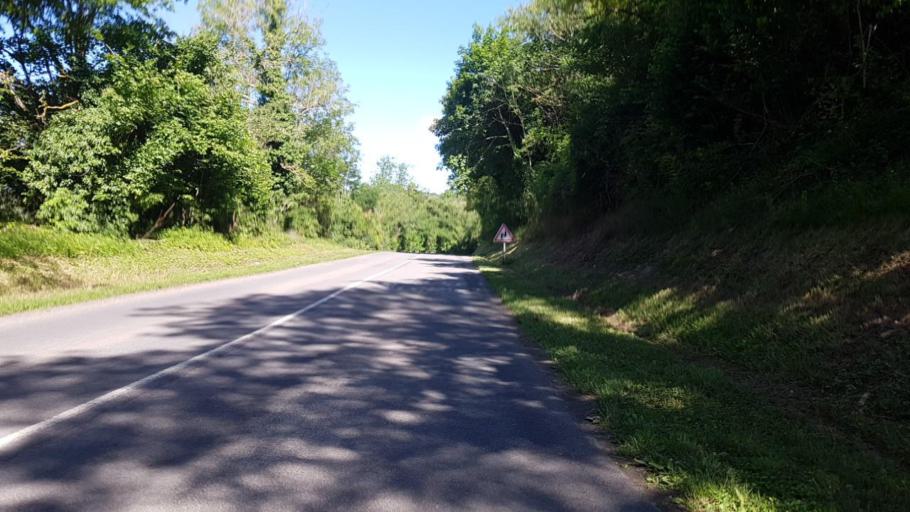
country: FR
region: Picardie
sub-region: Departement de l'Aisne
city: Charly-sur-Marne
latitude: 48.9768
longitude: 3.2496
